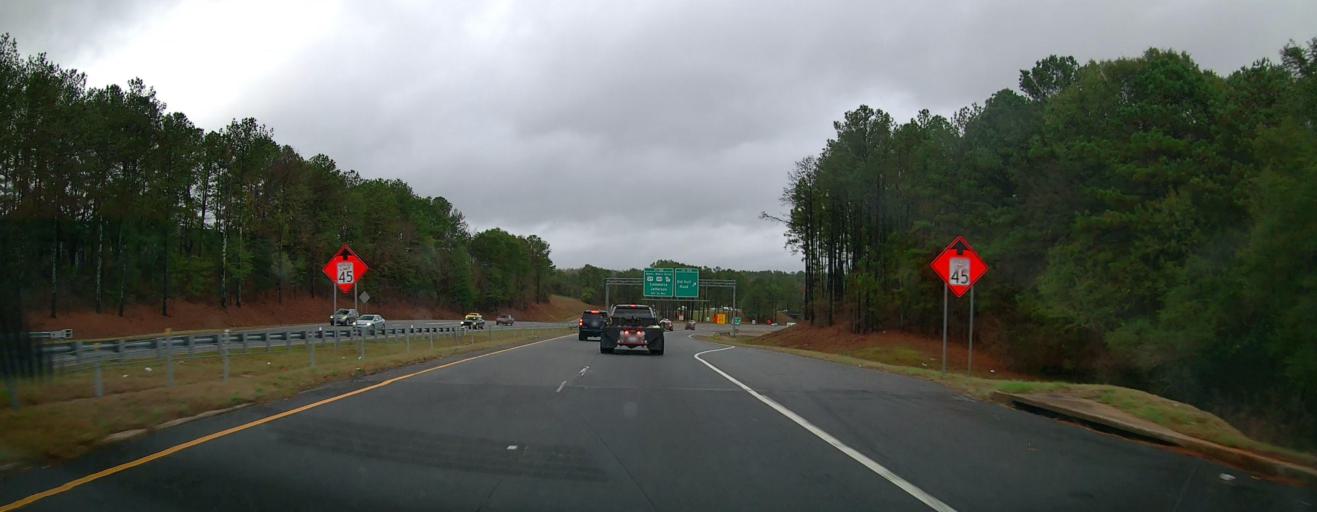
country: US
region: Georgia
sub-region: Clarke County
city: Athens
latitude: 33.9716
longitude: -83.3547
